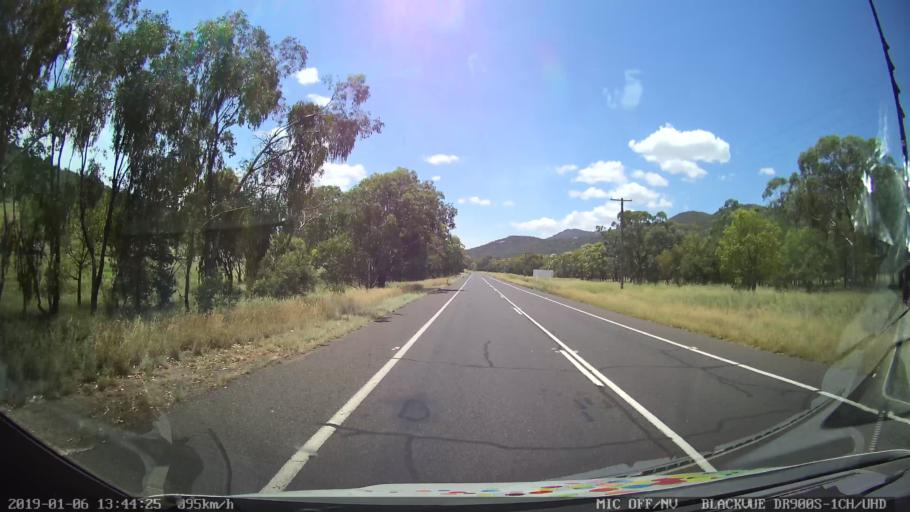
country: AU
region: New South Wales
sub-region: Tamworth Municipality
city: Kootingal
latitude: -31.0059
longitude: 151.0904
